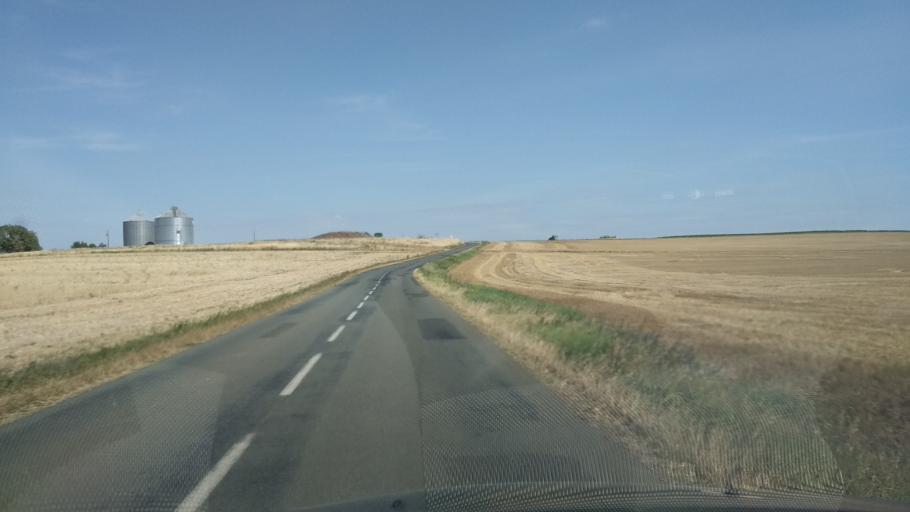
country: FR
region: Poitou-Charentes
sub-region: Departement de la Vienne
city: Vouille
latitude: 46.6842
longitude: 0.1640
